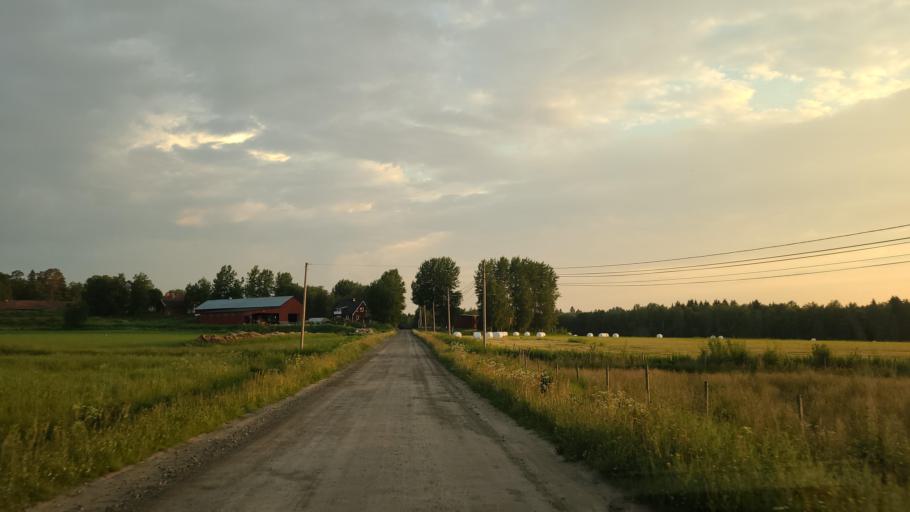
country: SE
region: Vaesterbotten
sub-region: Robertsfors Kommun
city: Robertsfors
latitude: 64.0655
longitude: 20.8701
